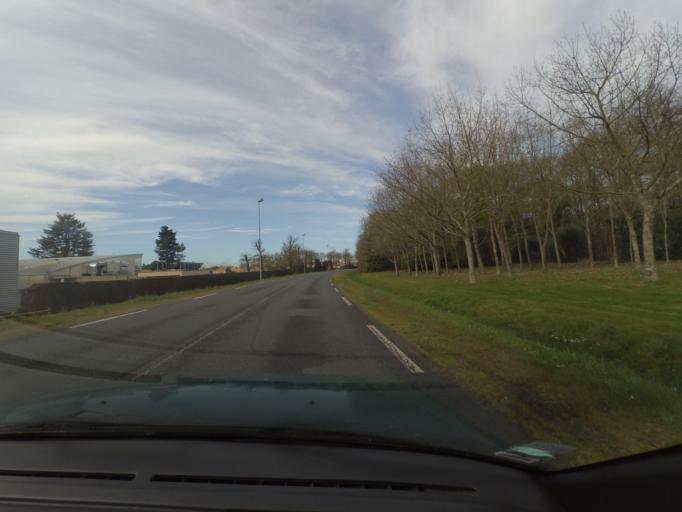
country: FR
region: Pays de la Loire
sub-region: Departement de la Loire-Atlantique
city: Aigrefeuille-sur-Maine
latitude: 47.0765
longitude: -1.4077
